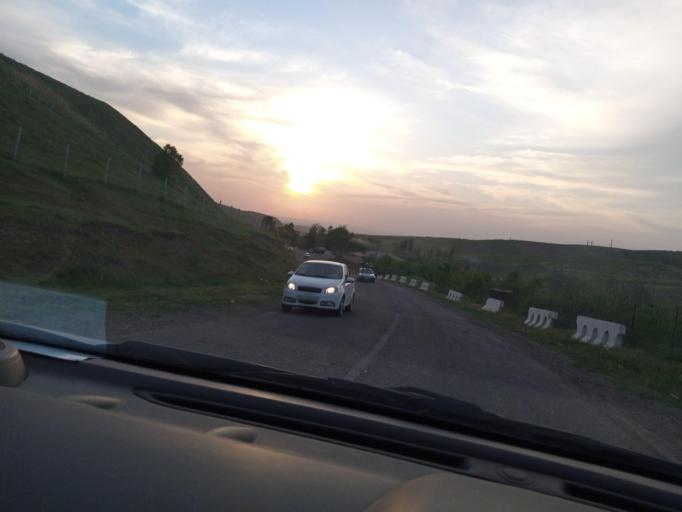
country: UZ
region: Toshkent
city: Parkent
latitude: 41.2416
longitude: 69.7321
